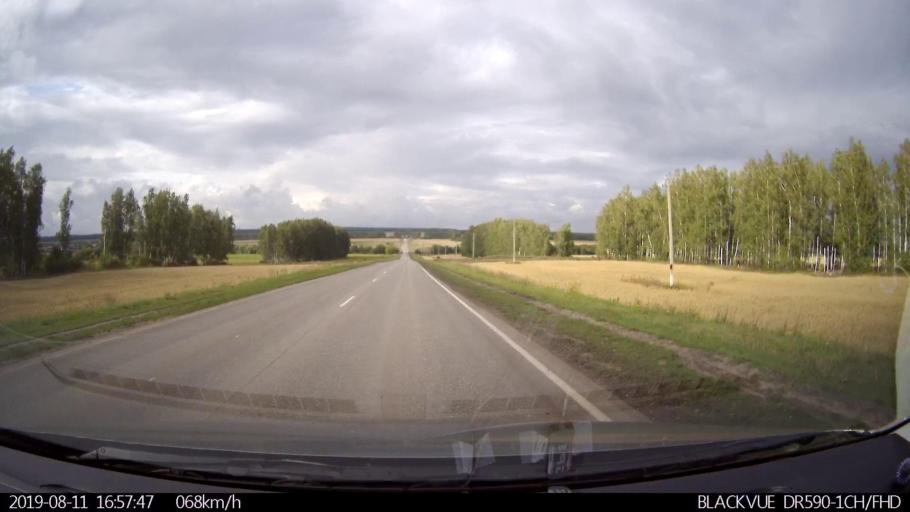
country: RU
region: Ulyanovsk
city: Mayna
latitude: 54.3007
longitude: 47.6533
